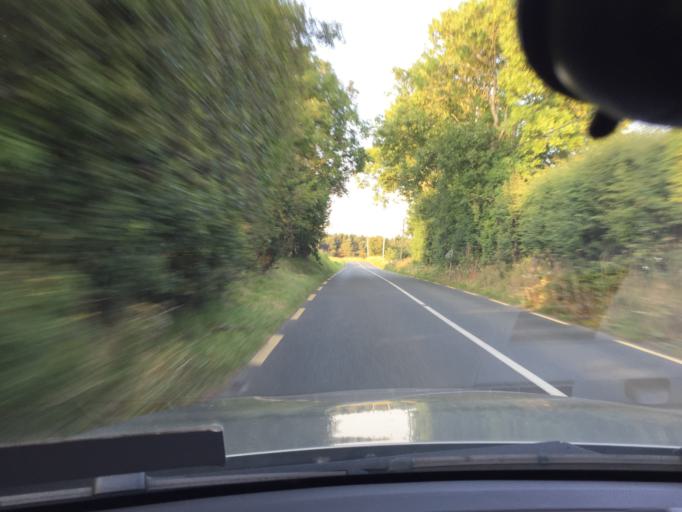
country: IE
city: Newtownmountkennedy
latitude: 53.0908
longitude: -6.2063
